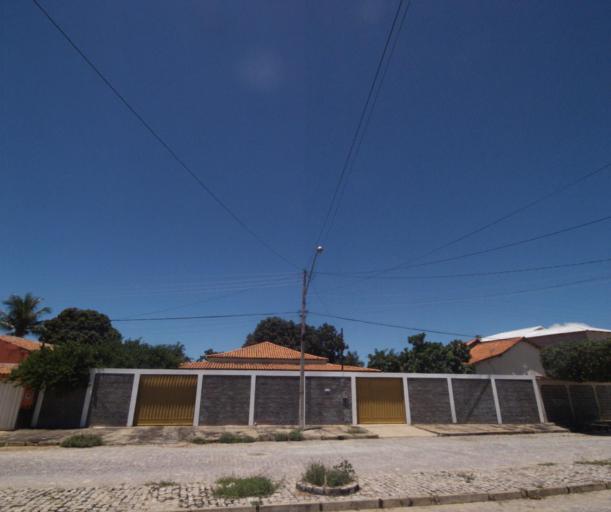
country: BR
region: Bahia
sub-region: Carinhanha
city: Carinhanha
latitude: -14.3055
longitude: -43.7694
